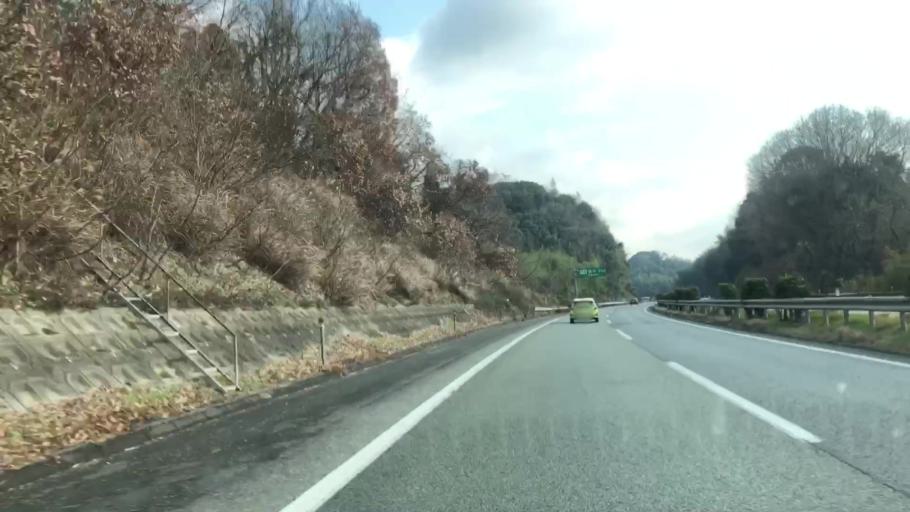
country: JP
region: Kumamoto
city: Tamana
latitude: 33.0008
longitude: 130.5895
